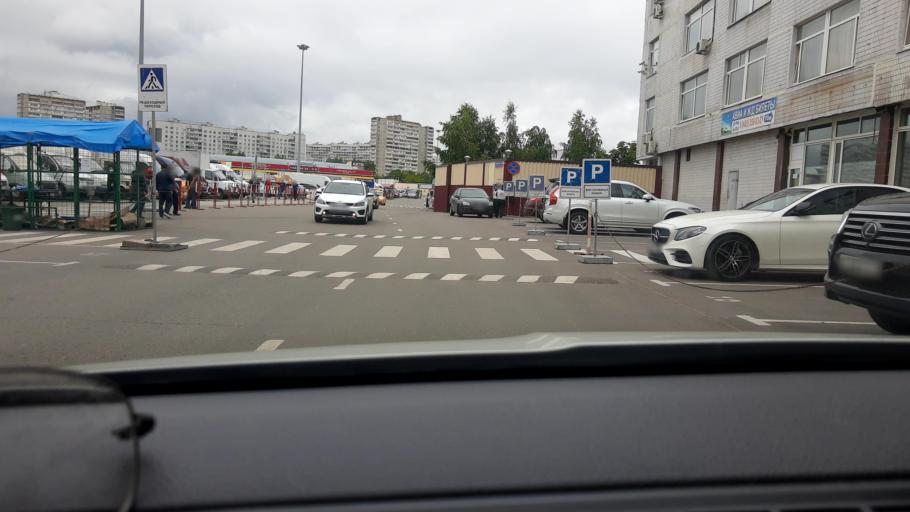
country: RU
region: Moscow
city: Lyublino
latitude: 55.6754
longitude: 37.7820
